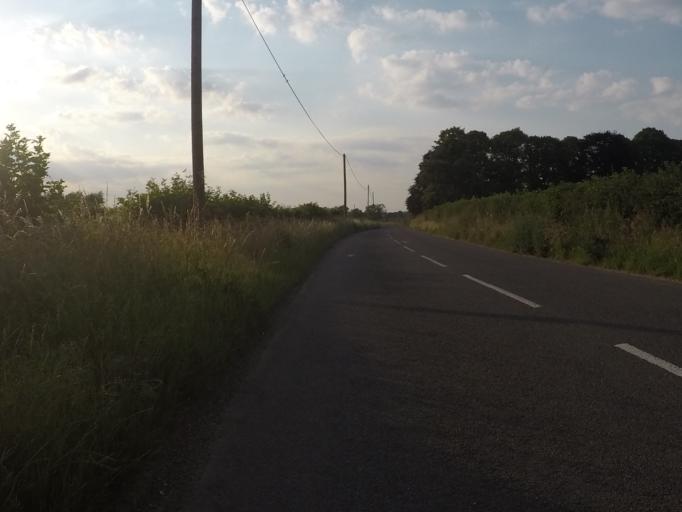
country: GB
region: England
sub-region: Oxfordshire
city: Charlbury
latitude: 51.8822
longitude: -1.4881
